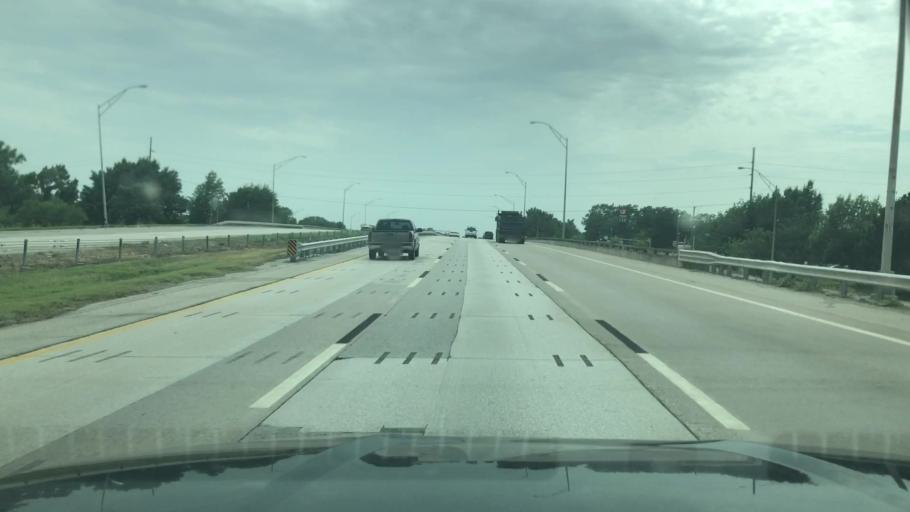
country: US
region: Oklahoma
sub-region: Tulsa County
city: Tulsa
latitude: 36.1570
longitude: -96.0184
